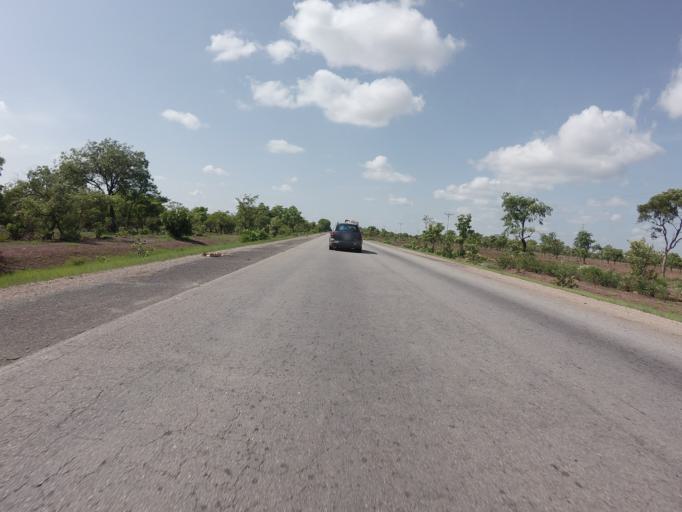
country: GH
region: Northern
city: Savelugu
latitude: 9.9559
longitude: -0.8345
